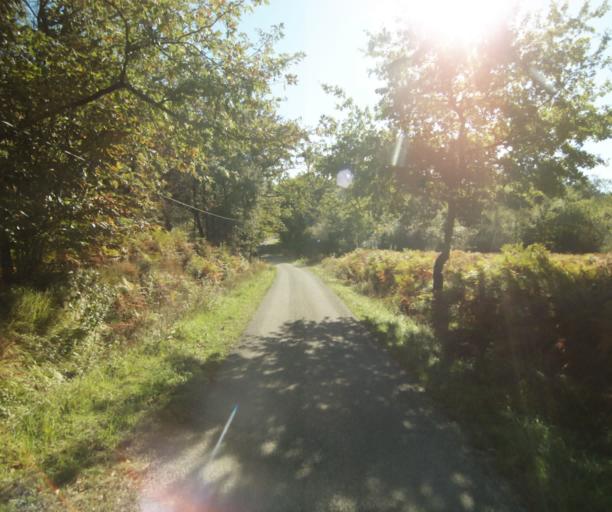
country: FR
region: Midi-Pyrenees
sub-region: Departement du Gers
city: Eauze
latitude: 43.8084
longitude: 0.1216
